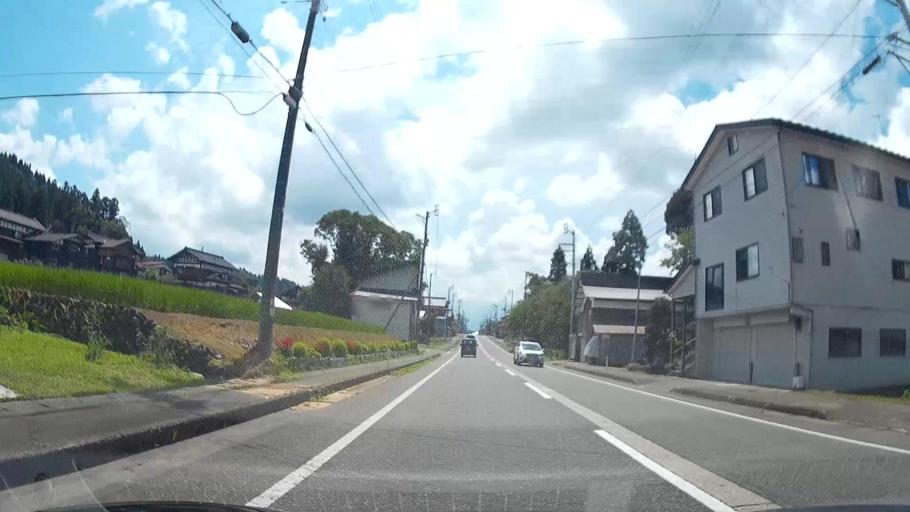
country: JP
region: Niigata
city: Tokamachi
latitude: 37.0598
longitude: 138.7062
